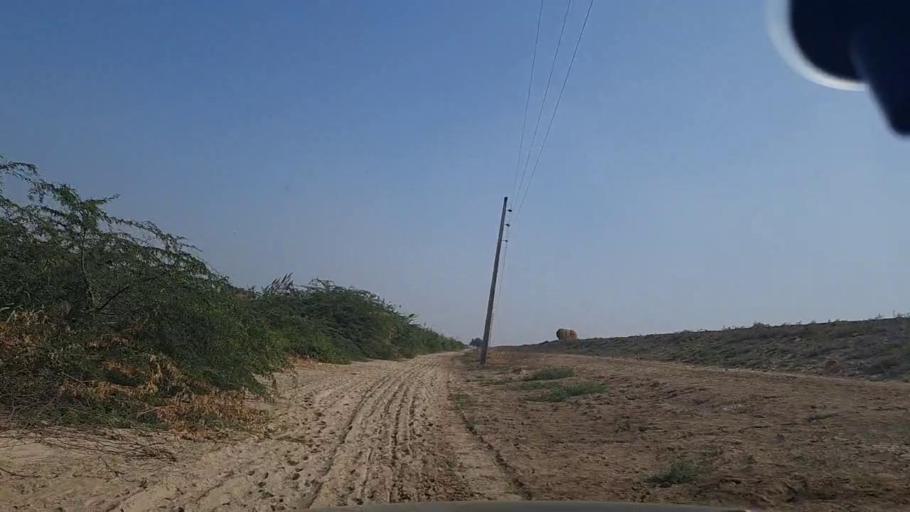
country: PK
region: Sindh
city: Chuhar Jamali
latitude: 24.4617
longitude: 67.8971
